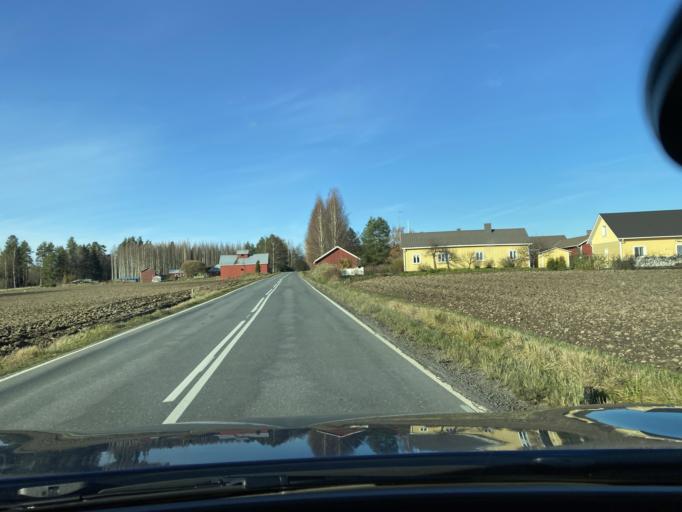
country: FI
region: Haeme
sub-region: Forssa
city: Tammela
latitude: 60.8357
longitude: 23.8382
